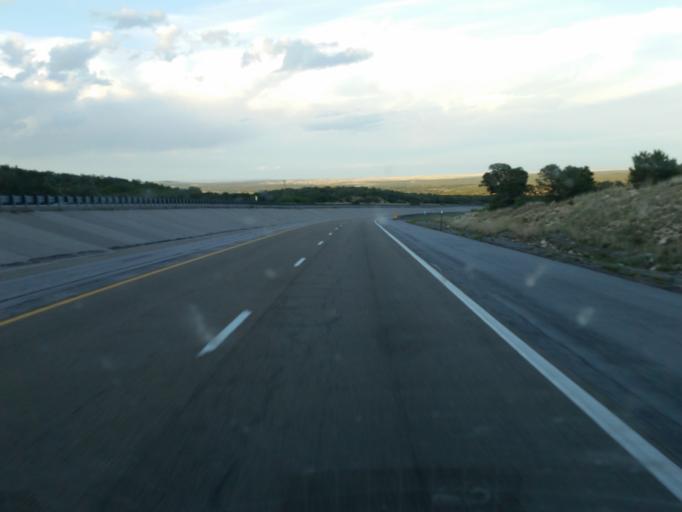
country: US
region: New Mexico
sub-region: Torrance County
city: Moriarty
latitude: 35.0040
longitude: -105.5457
